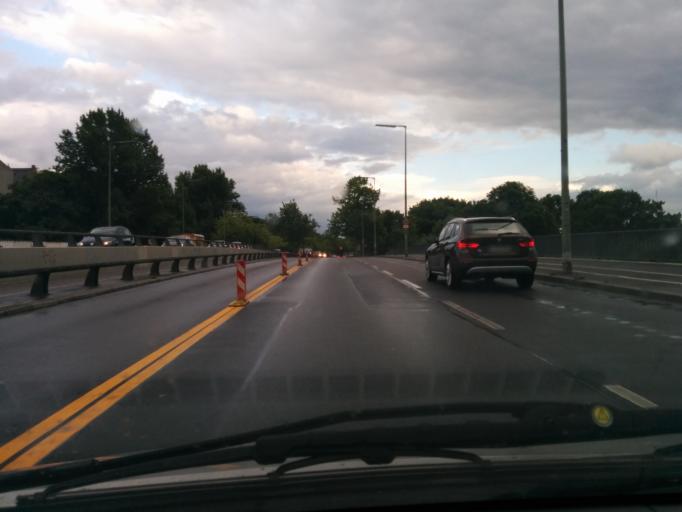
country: DE
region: Berlin
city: Spandau
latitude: 52.5321
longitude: 13.2005
